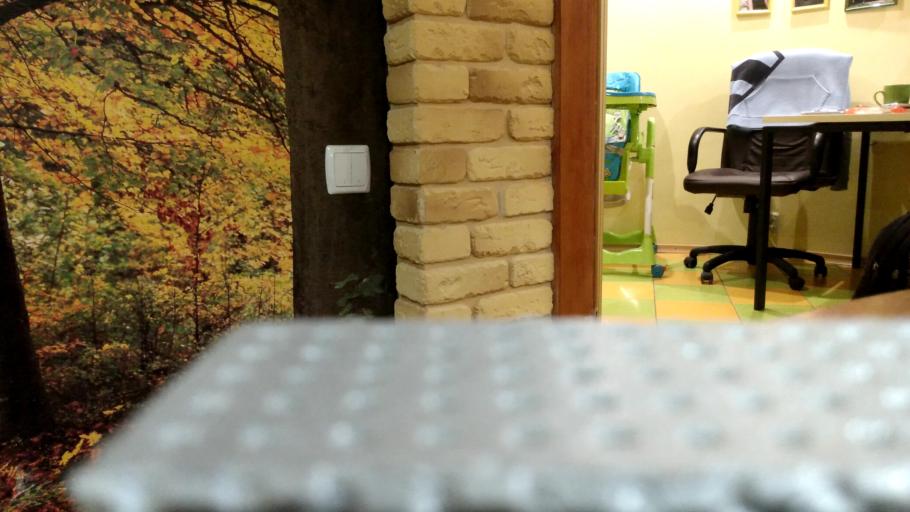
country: RU
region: Republic of Karelia
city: Pudozh
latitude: 61.9335
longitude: 37.6235
